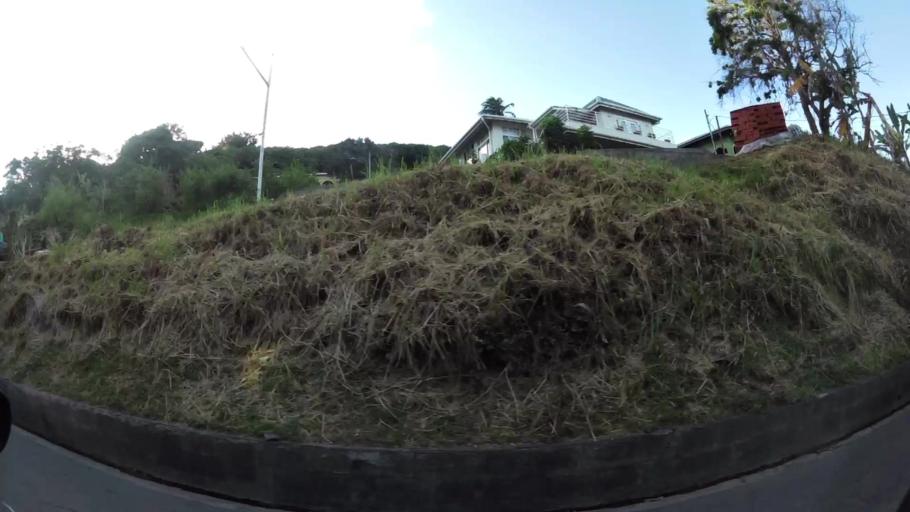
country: TT
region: Tobago
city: Scarborough
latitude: 11.1859
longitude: -60.6982
